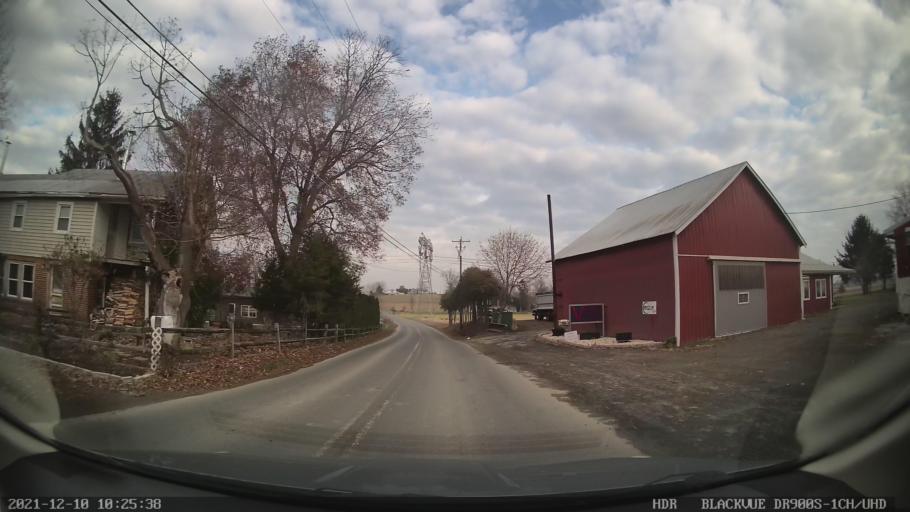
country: US
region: Pennsylvania
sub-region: Berks County
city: Topton
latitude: 40.4903
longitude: -75.7424
